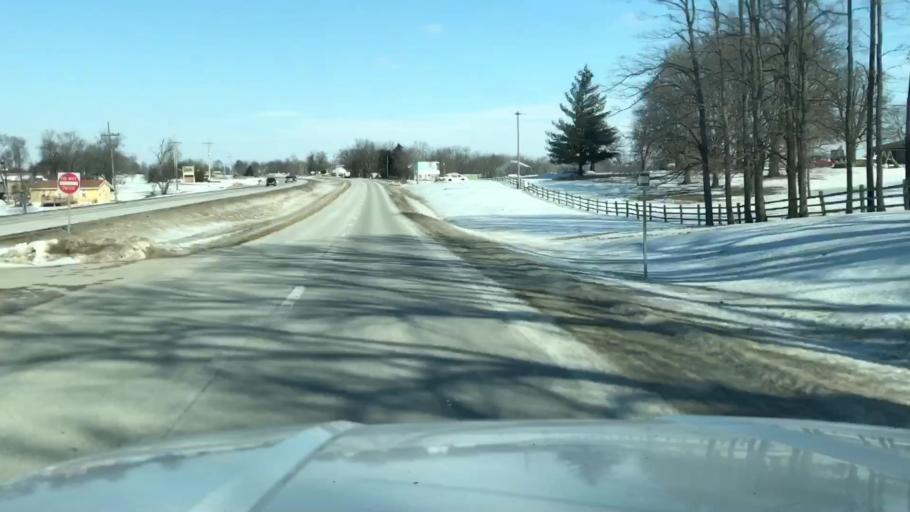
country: US
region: Missouri
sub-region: Andrew County
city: Savannah
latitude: 39.9051
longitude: -94.8096
